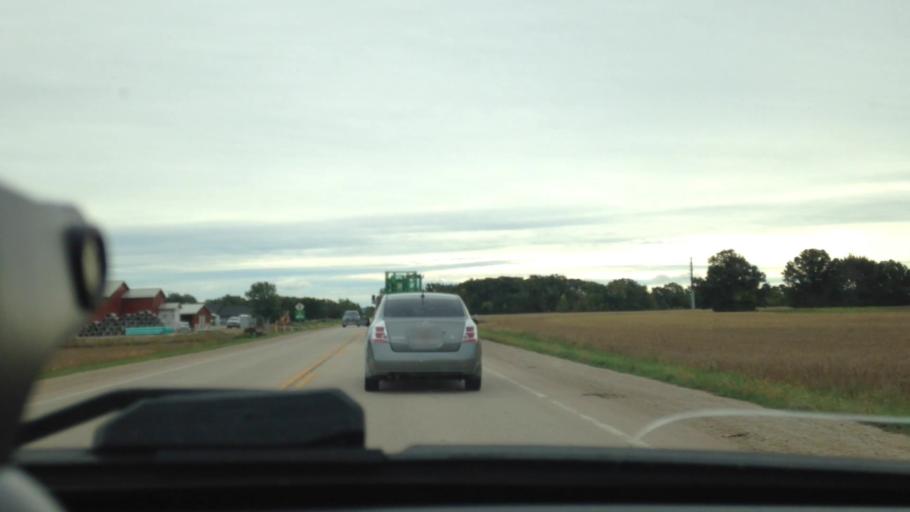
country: US
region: Wisconsin
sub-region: Fond du Lac County
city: North Fond du Lac
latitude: 43.8037
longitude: -88.5000
